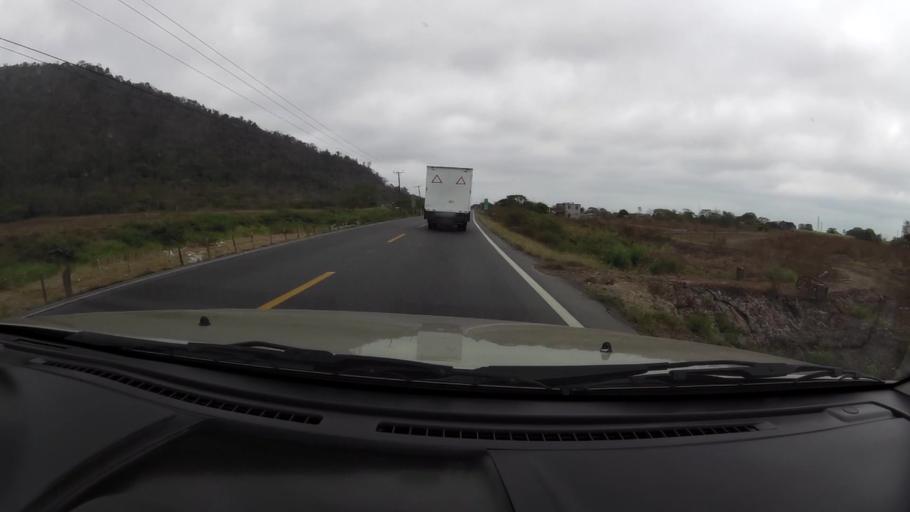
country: EC
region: Guayas
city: Naranjal
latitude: -2.4458
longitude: -79.6274
